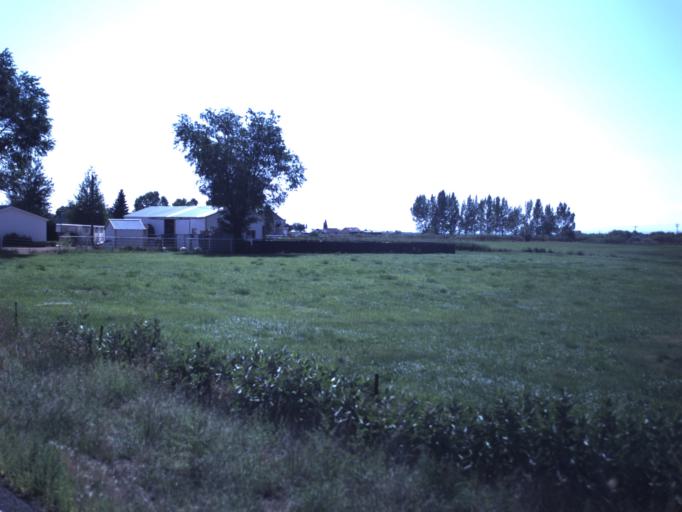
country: US
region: Utah
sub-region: Duchesne County
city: Duchesne
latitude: 40.3592
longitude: -110.2972
